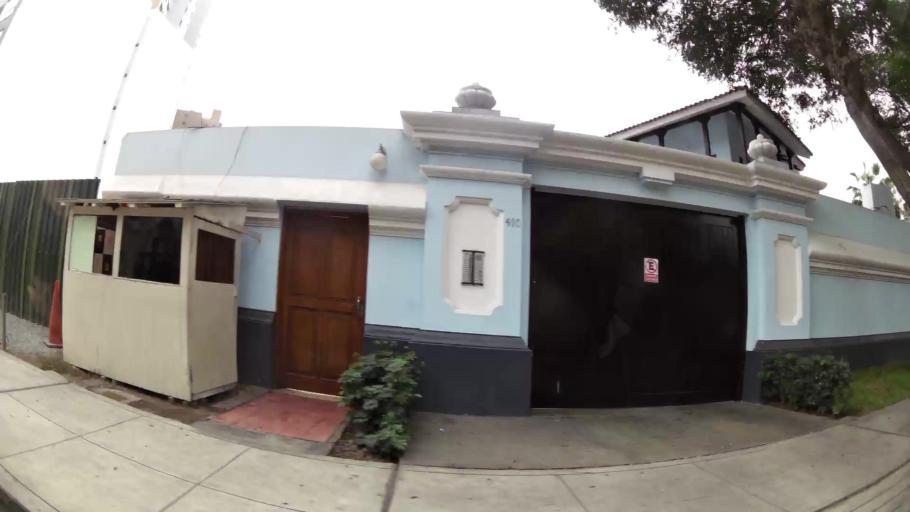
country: PE
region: Lima
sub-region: Lima
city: San Isidro
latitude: -12.0996
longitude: -77.0403
